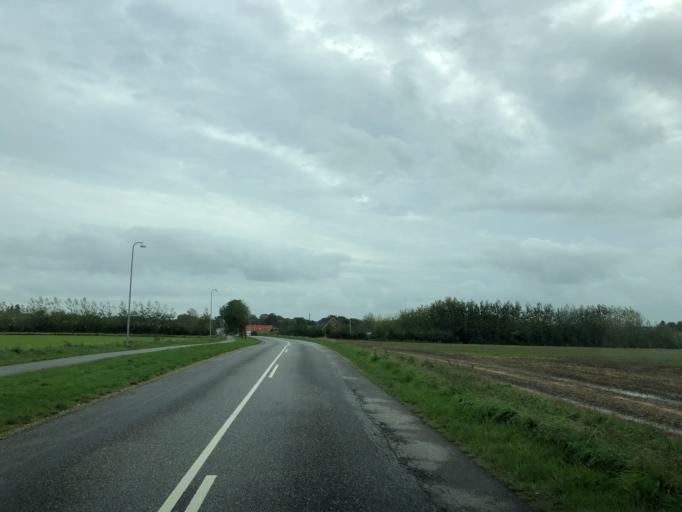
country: DK
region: Central Jutland
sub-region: Herning Kommune
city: Vildbjerg
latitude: 56.1845
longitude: 8.7457
